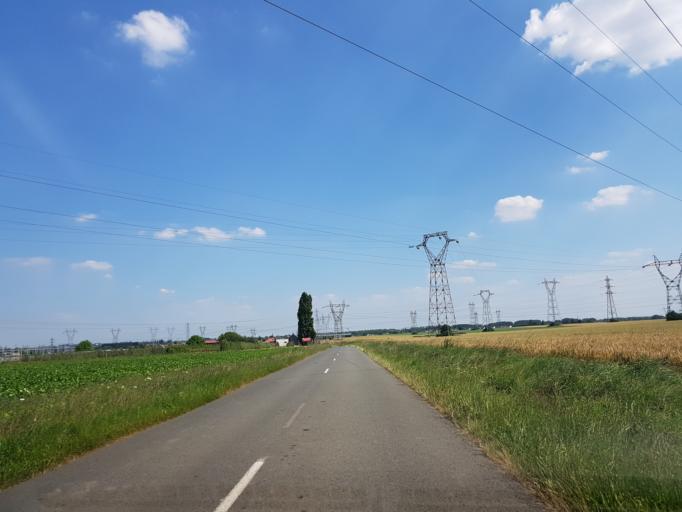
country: FR
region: Nord-Pas-de-Calais
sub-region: Departement du Nord
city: Roeulx
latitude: 50.3204
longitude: 3.3206
